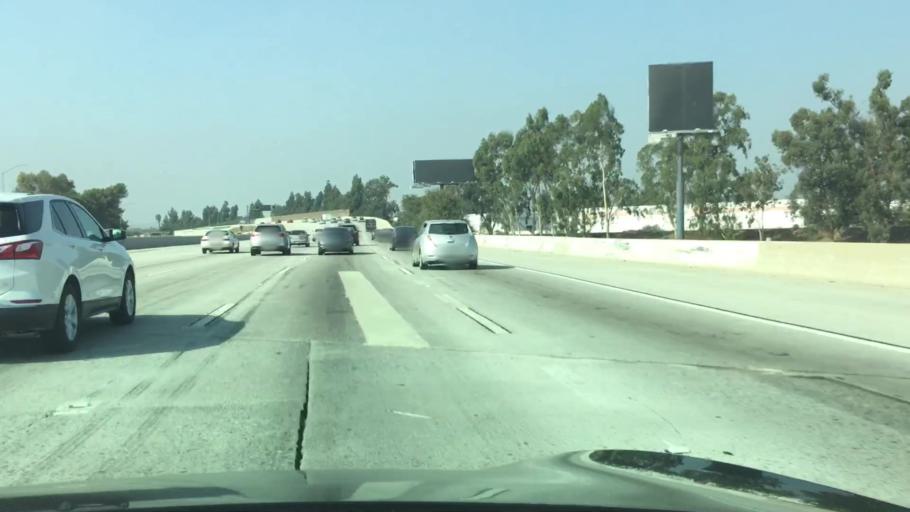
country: US
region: California
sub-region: Los Angeles County
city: South El Monte
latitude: 34.0706
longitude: -118.0477
